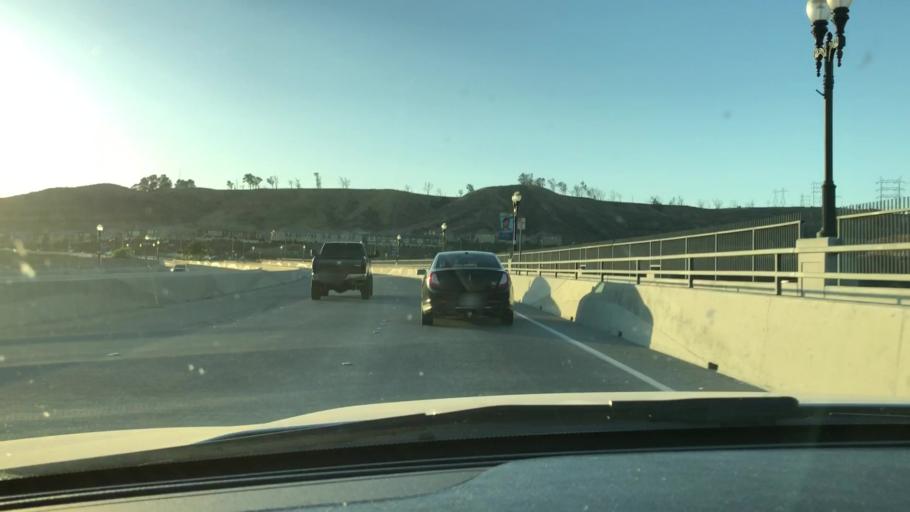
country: US
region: California
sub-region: Los Angeles County
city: Santa Clarita
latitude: 34.4252
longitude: -118.5044
